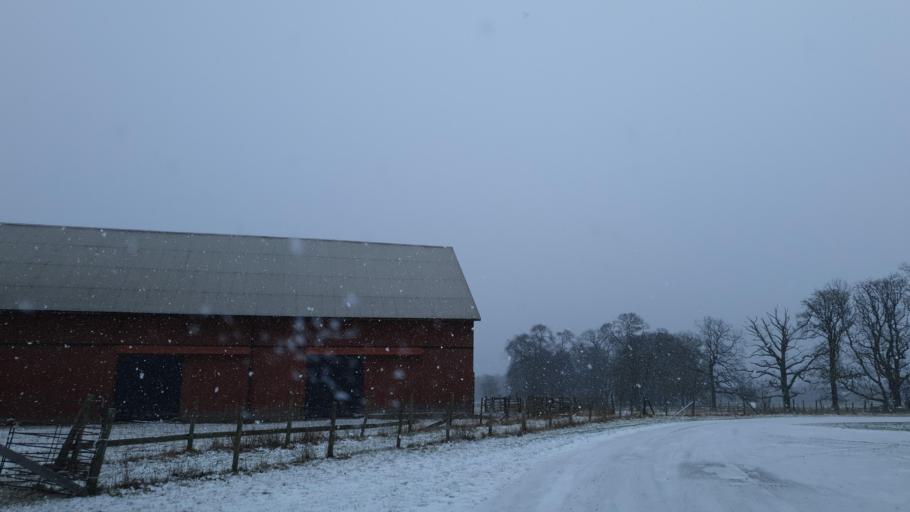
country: SE
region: Gotland
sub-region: Gotland
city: Visby
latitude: 57.5165
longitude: 18.4601
